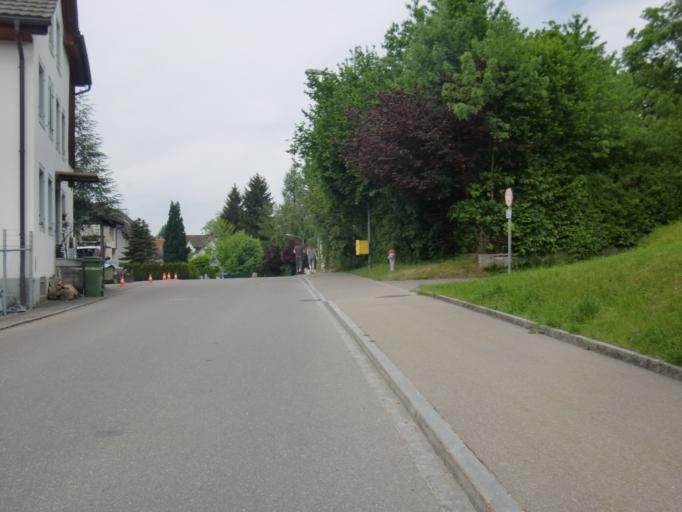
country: CH
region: Zurich
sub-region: Bezirk Hinwil
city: Tann / Tann (Dorfkern)
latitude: 47.2663
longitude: 8.8454
